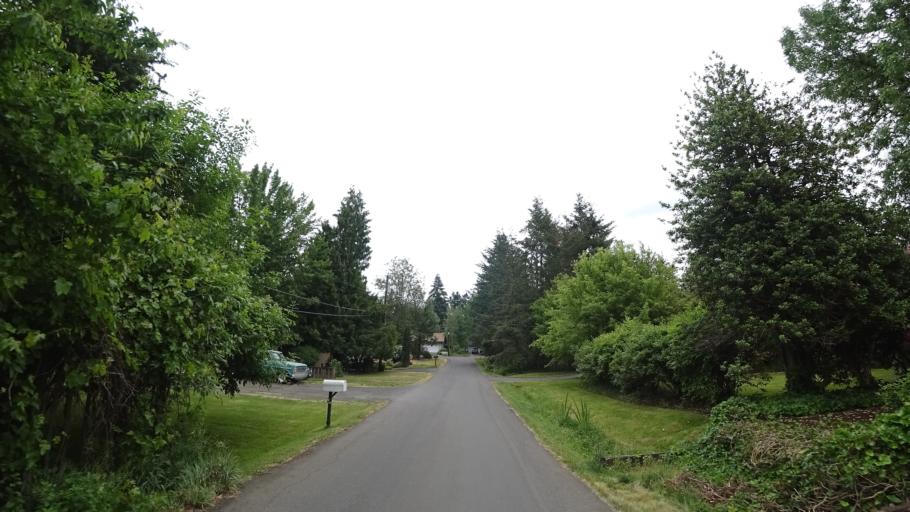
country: US
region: Oregon
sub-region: Washington County
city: Garden Home-Whitford
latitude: 45.4630
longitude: -122.7670
